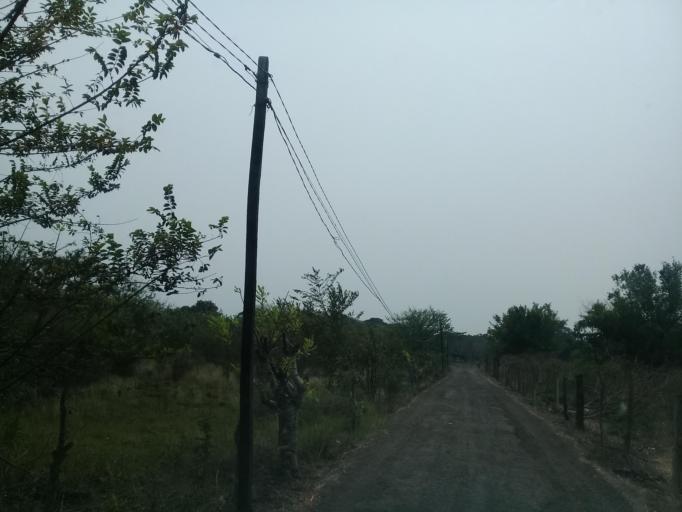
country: MX
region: Veracruz
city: Paso del Toro
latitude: 18.9819
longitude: -96.1763
